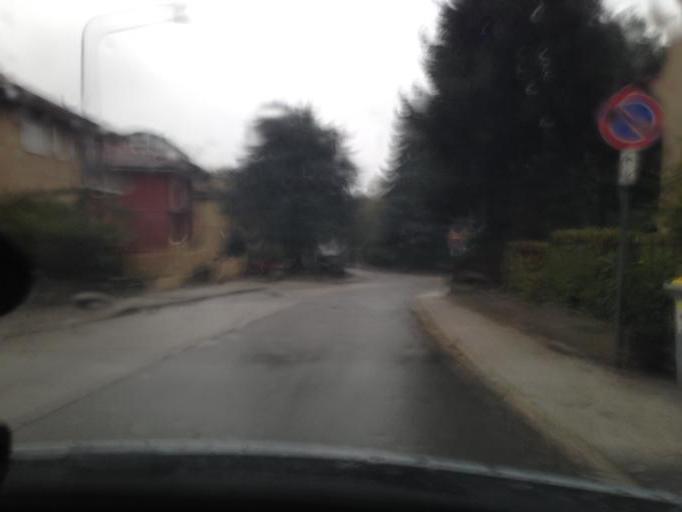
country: IT
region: Trentino-Alto Adige
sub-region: Provincia di Trento
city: Rovereto
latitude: 45.9009
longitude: 11.0462
